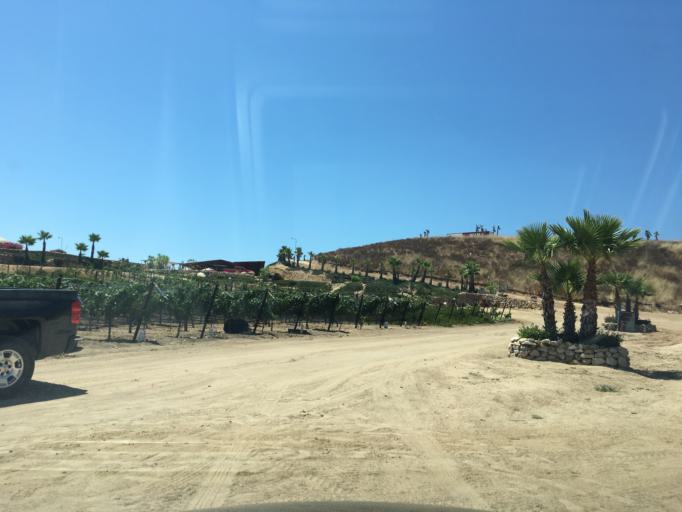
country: MX
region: Baja California
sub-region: Ensenada
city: Rancho Verde
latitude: 32.0281
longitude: -116.6226
